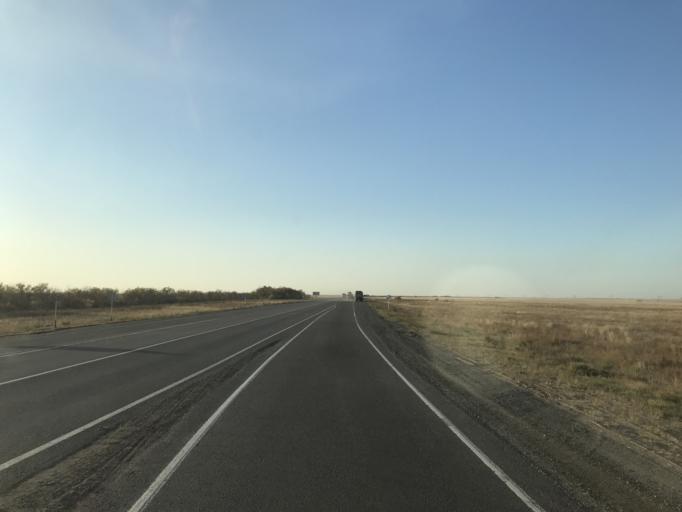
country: KZ
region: Pavlodar
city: Leninskiy
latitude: 52.1557
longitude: 76.8180
